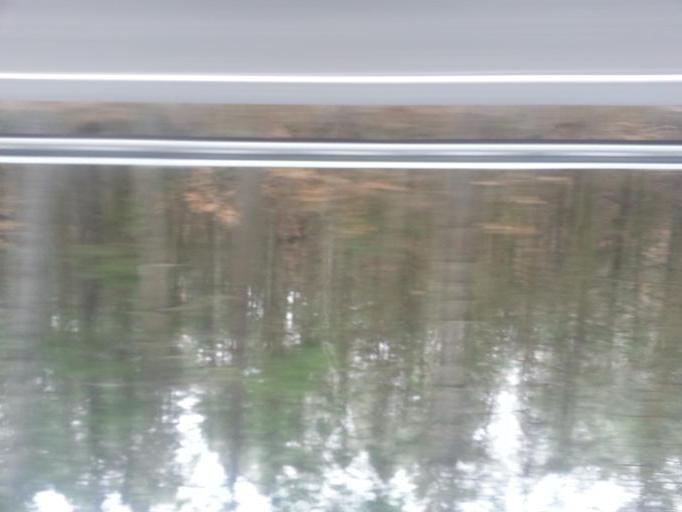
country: US
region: Tennessee
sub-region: Morgan County
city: Wartburg
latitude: 36.0403
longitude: -84.5271
